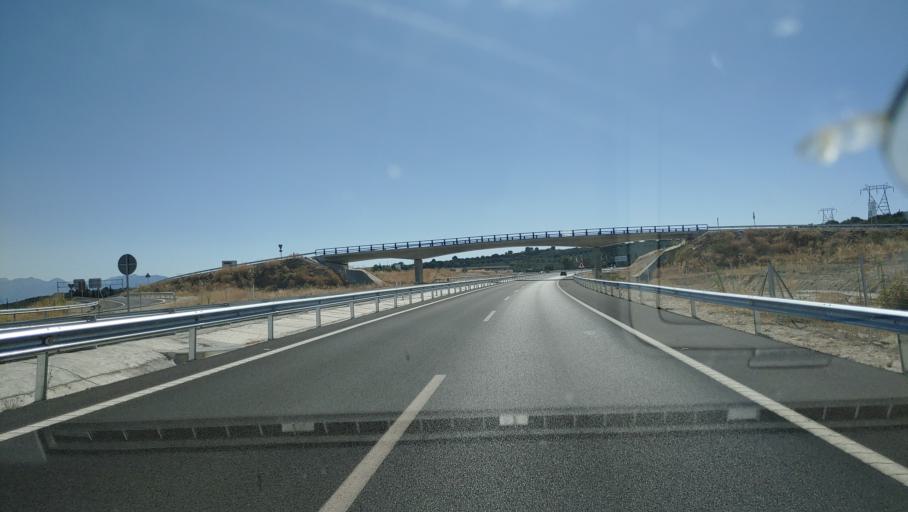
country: ES
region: Andalusia
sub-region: Provincia de Jaen
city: Sabiote
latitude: 38.0334
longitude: -3.3302
